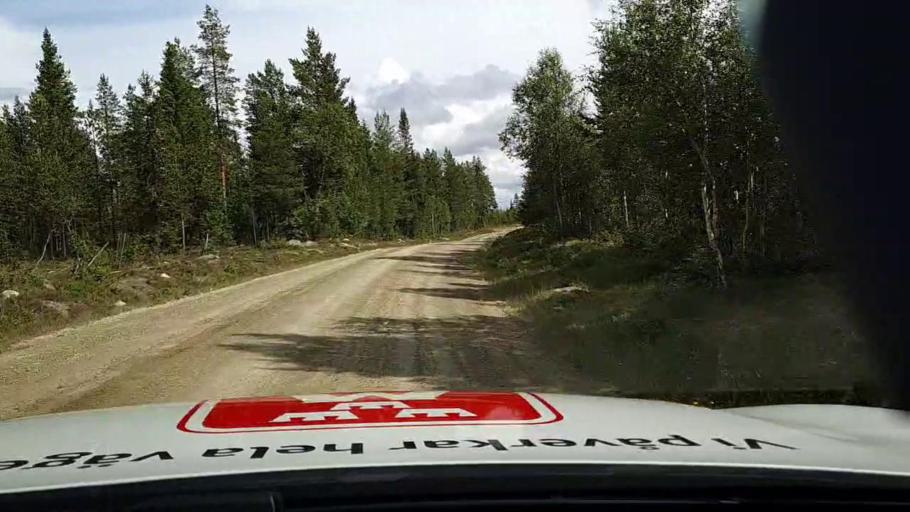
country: SE
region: Jaemtland
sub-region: Are Kommun
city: Jarpen
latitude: 62.5473
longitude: 13.4674
